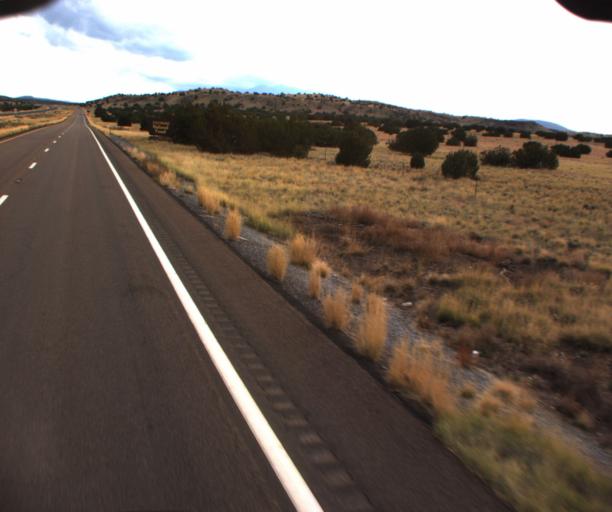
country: US
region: Arizona
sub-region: Coconino County
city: Flagstaff
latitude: 35.5306
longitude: -111.5416
